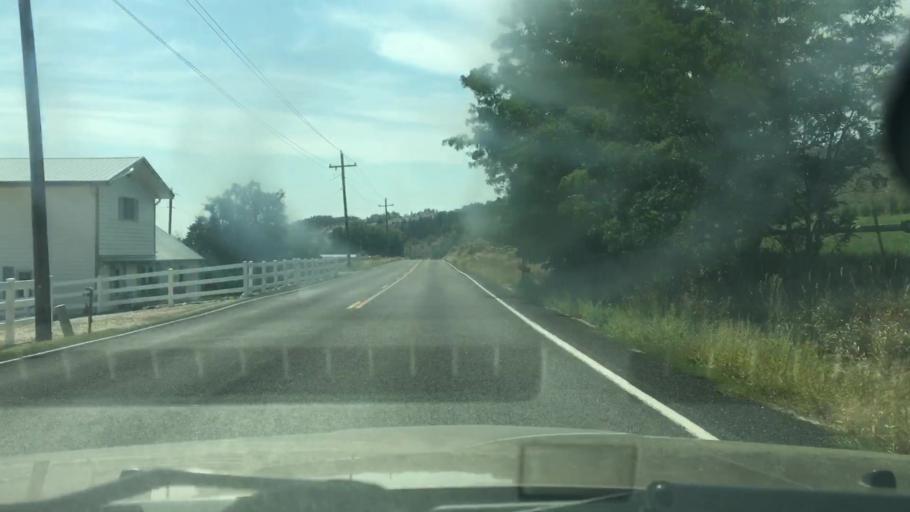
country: US
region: Colorado
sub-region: Larimer County
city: Loveland
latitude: 40.4622
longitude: -105.2067
